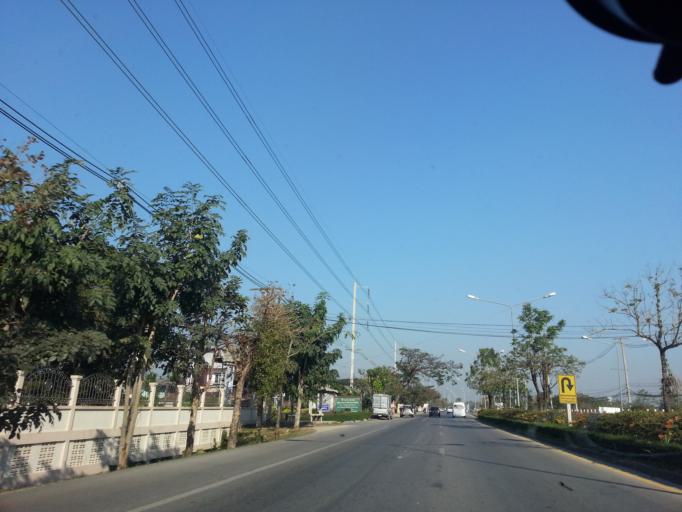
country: TH
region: Chiang Mai
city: San Sai
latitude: 18.9080
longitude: 99.0019
